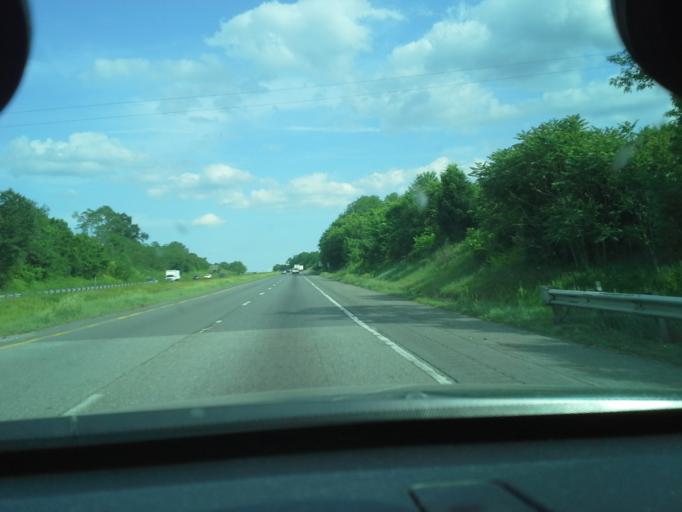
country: US
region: Maryland
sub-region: Frederick County
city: Middletown
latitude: 39.4801
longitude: -77.5387
